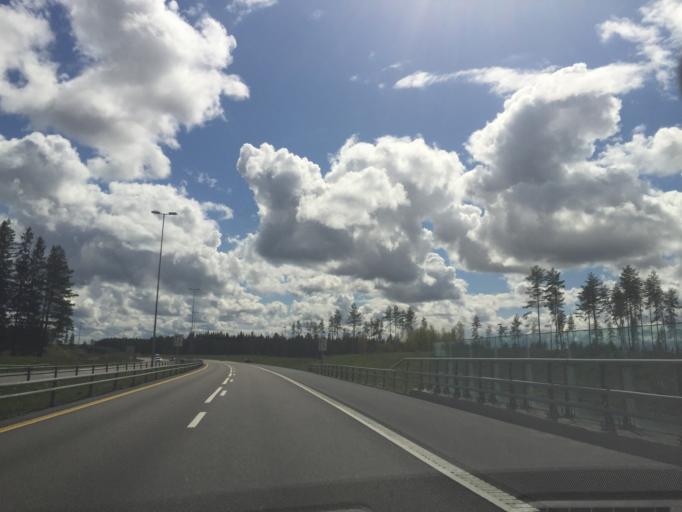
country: NO
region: Akershus
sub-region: Eidsvoll
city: Raholt
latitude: 60.2305
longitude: 11.1732
